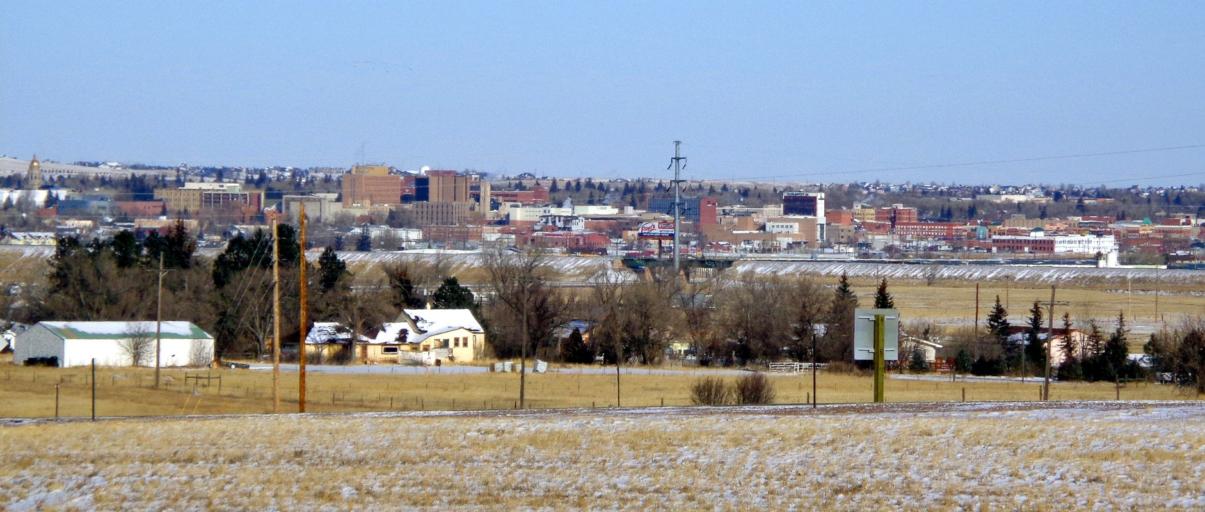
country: US
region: Wyoming
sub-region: Laramie County
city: South Greeley
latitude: 41.0993
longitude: -104.8526
